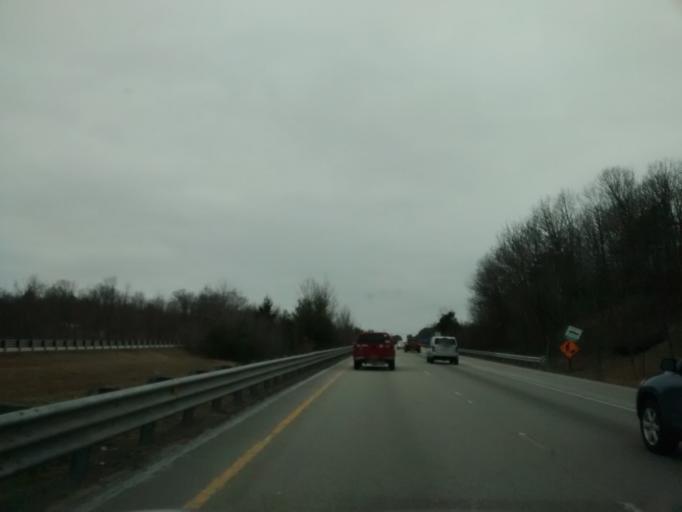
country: US
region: Massachusetts
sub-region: Worcester County
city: Westminster
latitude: 42.5465
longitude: -71.9042
